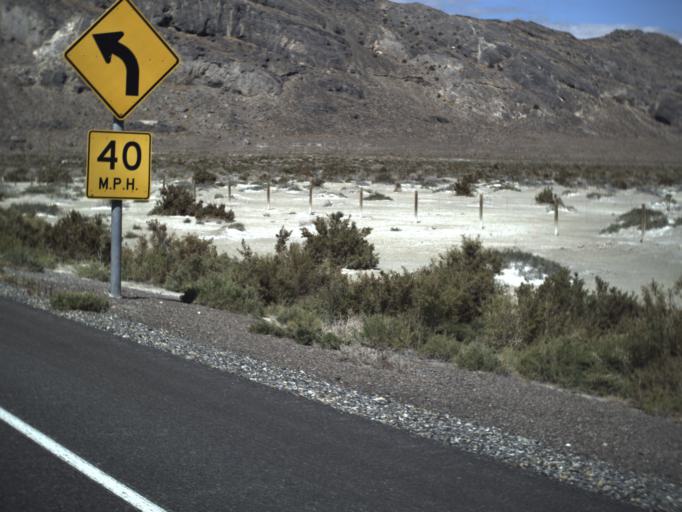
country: US
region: Utah
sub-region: Tooele County
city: Wendover
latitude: 40.7483
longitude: -114.0081
